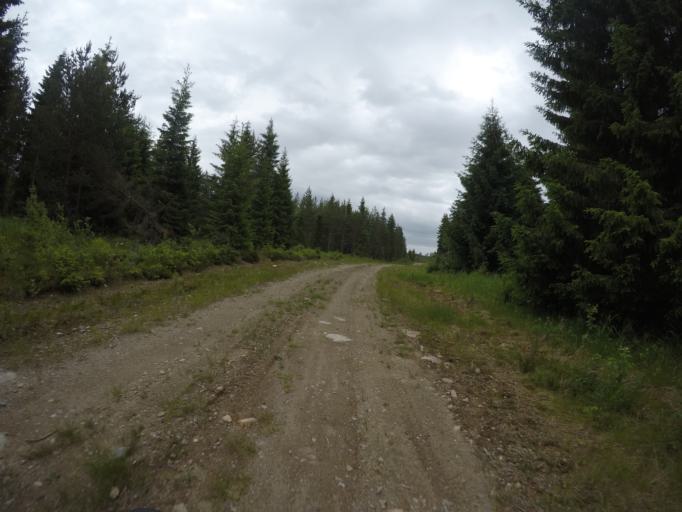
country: SE
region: Dalarna
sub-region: Ludvika Kommun
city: Abborrberget
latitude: 60.0612
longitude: 14.5642
